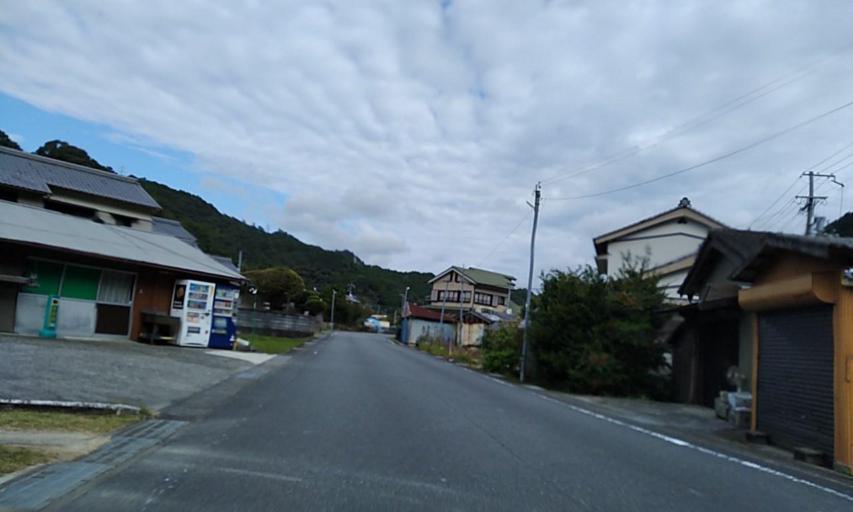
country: JP
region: Wakayama
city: Shingu
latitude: 33.5377
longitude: 135.8197
